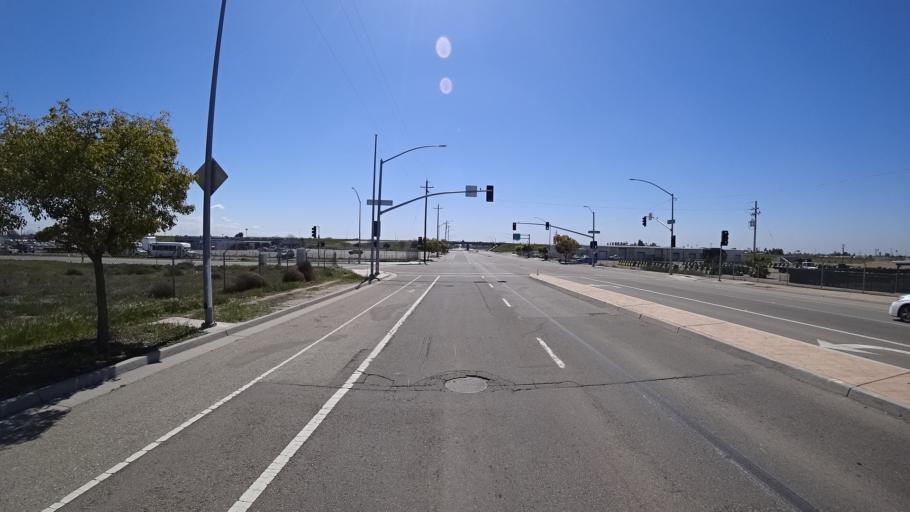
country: US
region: California
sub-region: Fresno County
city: West Park
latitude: 36.7417
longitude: -119.8443
